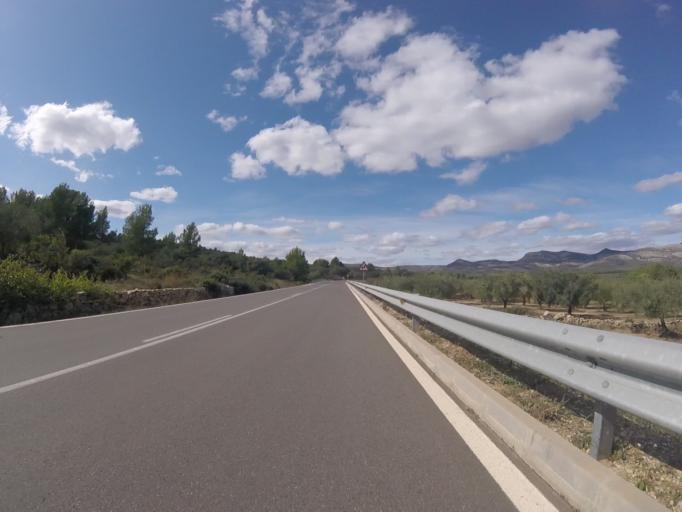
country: ES
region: Valencia
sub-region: Provincia de Castello
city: Chert/Xert
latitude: 40.4383
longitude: 0.1148
